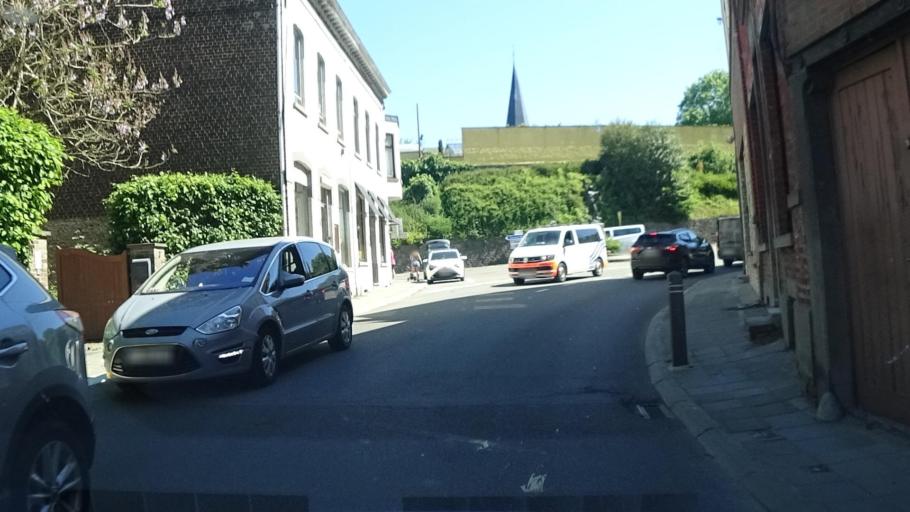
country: BE
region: Wallonia
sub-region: Province du Brabant Wallon
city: Court-Saint-Etienne
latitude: 50.6441
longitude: 4.5677
